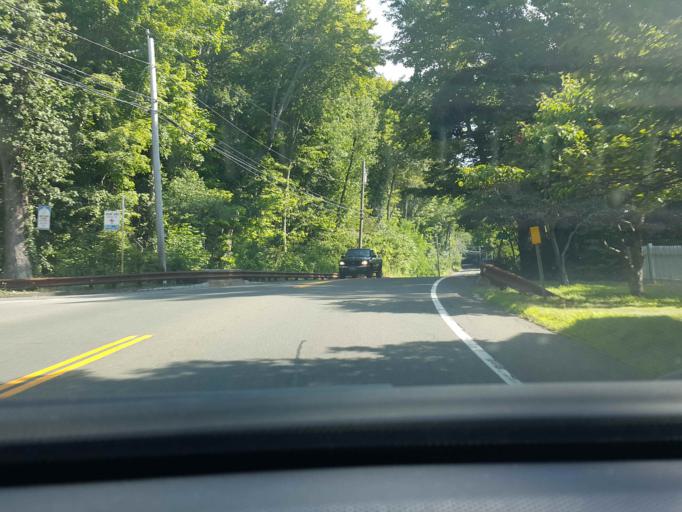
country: US
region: Connecticut
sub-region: New Haven County
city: North Branford
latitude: 41.3685
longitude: -72.7192
